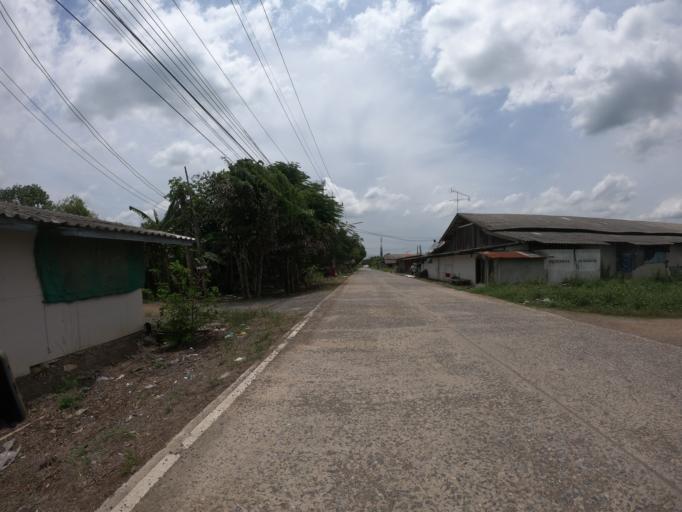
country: TH
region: Pathum Thani
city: Ban Lam Luk Ka
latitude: 13.9845
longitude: 100.8542
